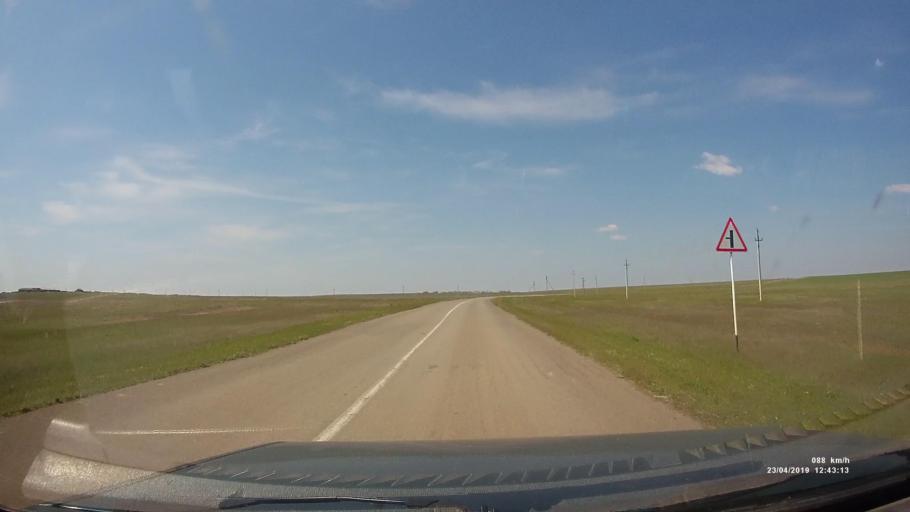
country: RU
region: Kalmykiya
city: Yashalta
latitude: 46.4622
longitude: 42.6531
